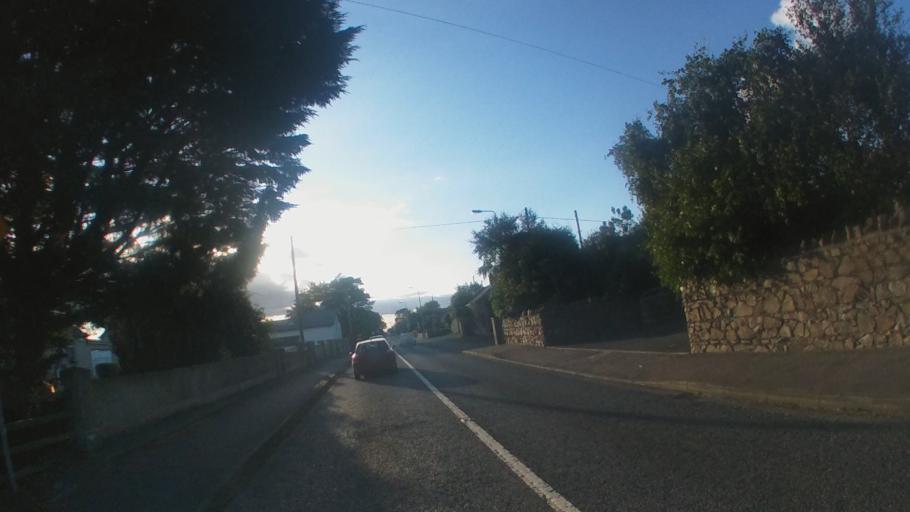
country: IE
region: Leinster
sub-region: Lu
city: Carlingford
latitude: 53.9992
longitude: -6.2593
